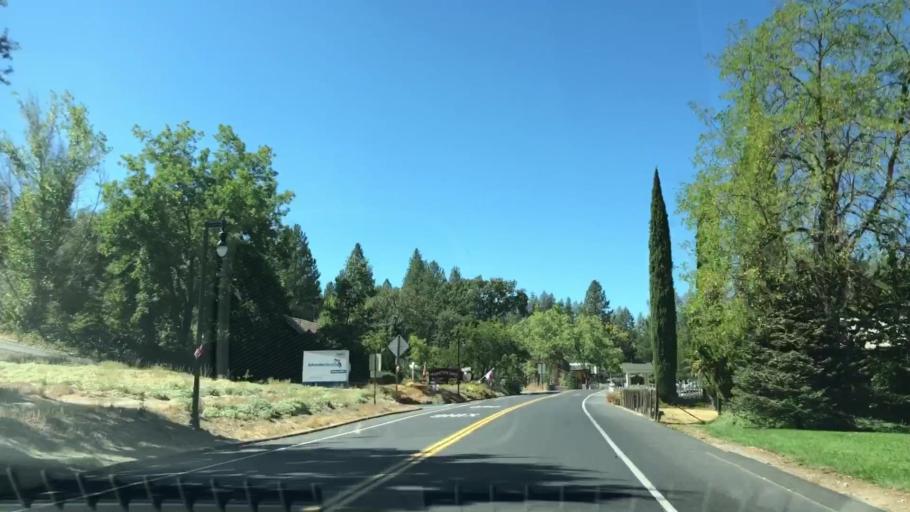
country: US
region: California
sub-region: Tuolumne County
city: Tuolumne City
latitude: 37.8383
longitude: -120.2316
